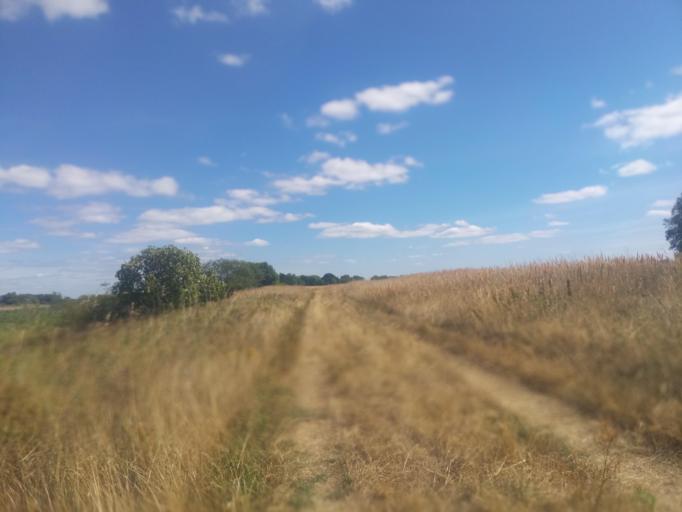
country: DE
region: Lower Saxony
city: Tosterglope
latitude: 53.2548
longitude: 10.8304
